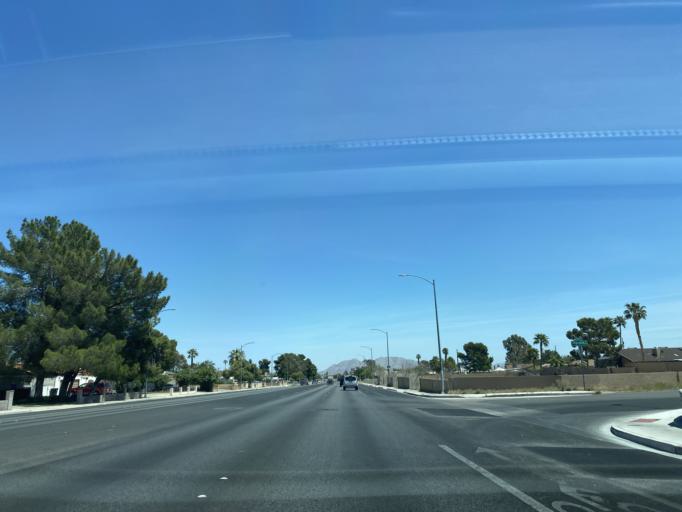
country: US
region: Nevada
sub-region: Clark County
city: Las Vegas
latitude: 36.1955
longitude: -115.2132
